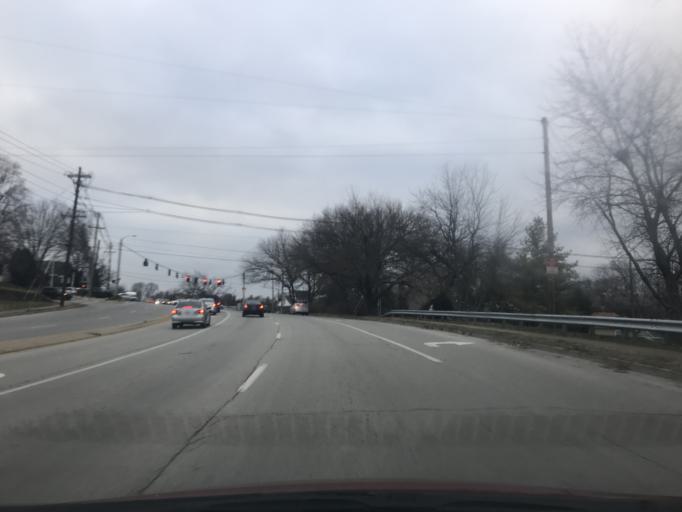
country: US
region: Kentucky
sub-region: Jefferson County
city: Audubon Park
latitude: 38.2232
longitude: -85.7294
